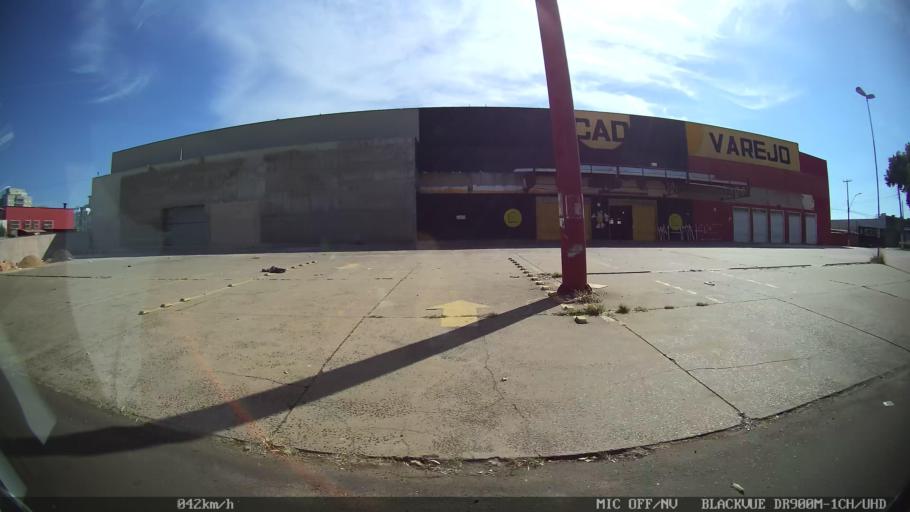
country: BR
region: Sao Paulo
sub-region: Franca
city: Franca
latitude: -20.5244
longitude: -47.4108
